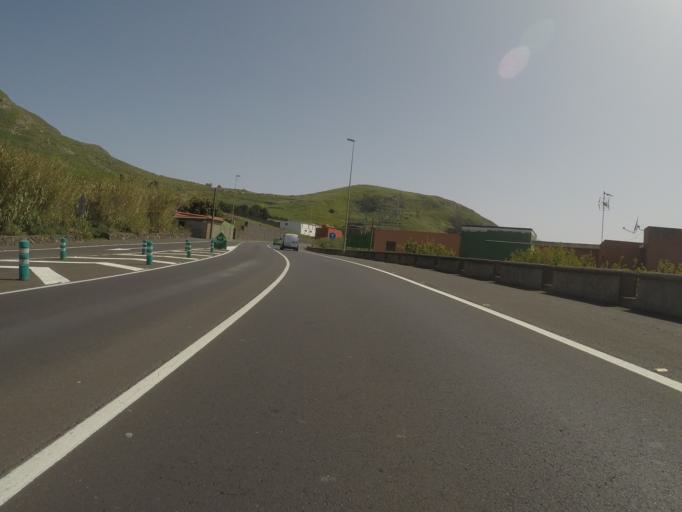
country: ES
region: Canary Islands
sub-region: Provincia de Santa Cruz de Tenerife
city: Tegueste
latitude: 28.5258
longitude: -16.2857
